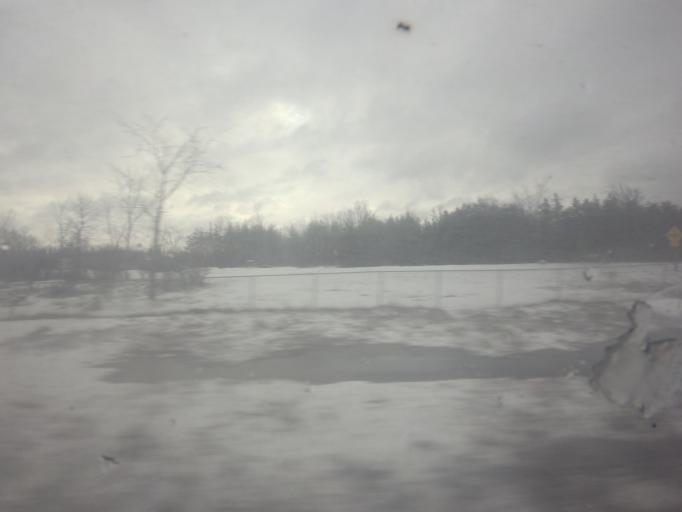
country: CA
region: Ontario
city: Bells Corners
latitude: 45.1192
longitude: -75.8698
